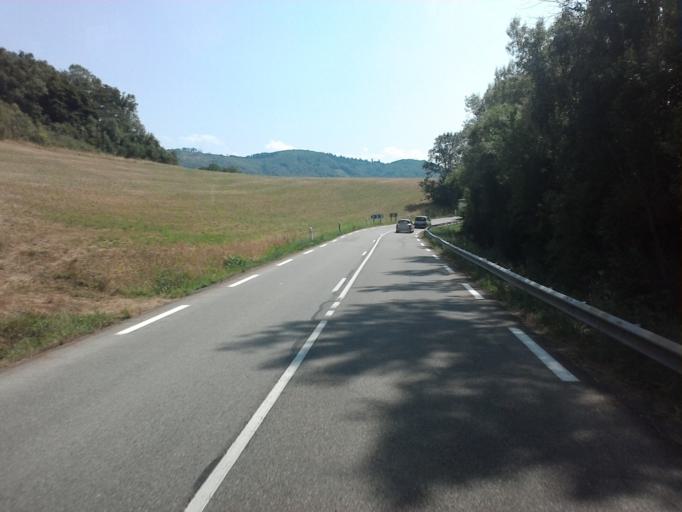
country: FR
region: Rhone-Alpes
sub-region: Departement de l'Isere
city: Bilieu
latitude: 45.4387
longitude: 5.5657
